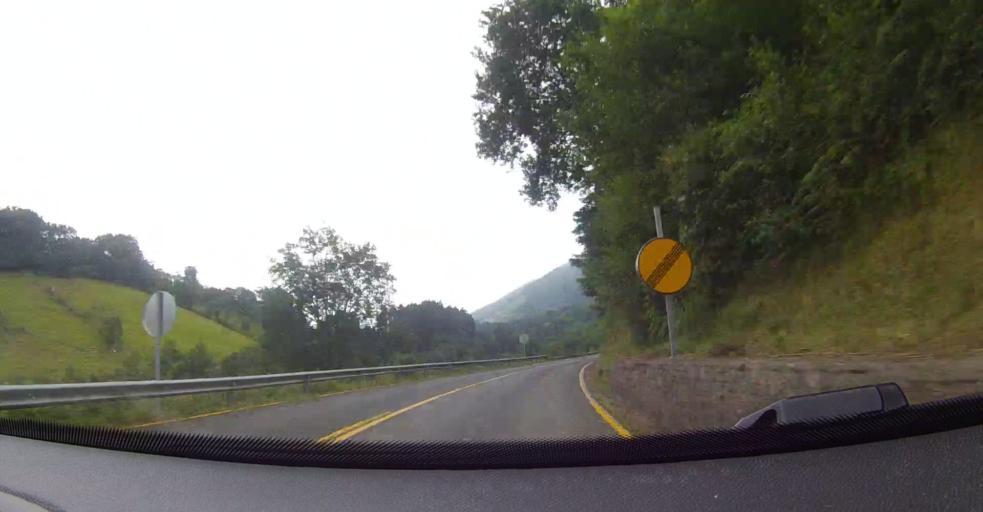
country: ES
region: Basque Country
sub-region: Bizkaia
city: Balmaseda
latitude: 43.2415
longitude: -3.2093
